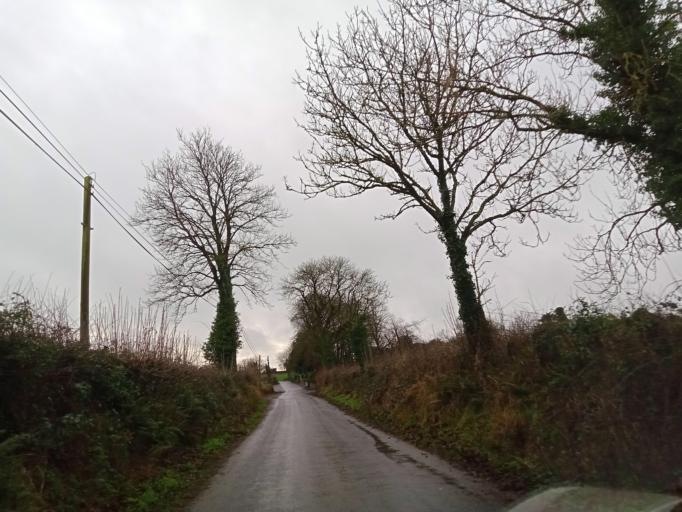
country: IE
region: Munster
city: Fethard
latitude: 52.5590
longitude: -7.6952
